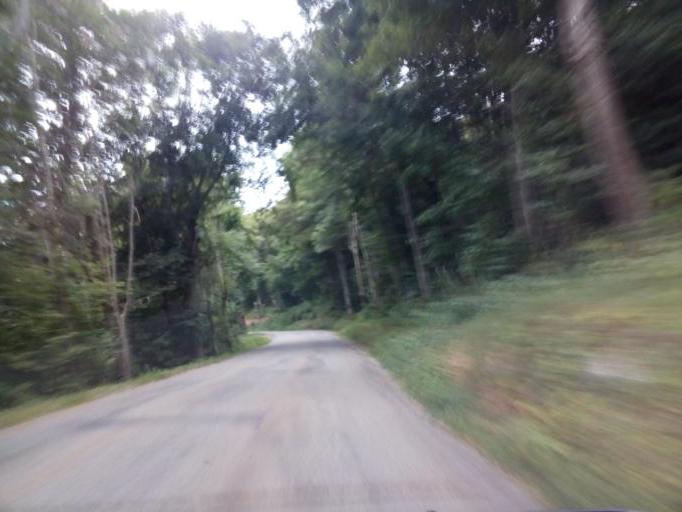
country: FR
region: Rhone-Alpes
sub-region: Departement de l'Isere
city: Pierre-Chatel
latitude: 44.9768
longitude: 5.7899
